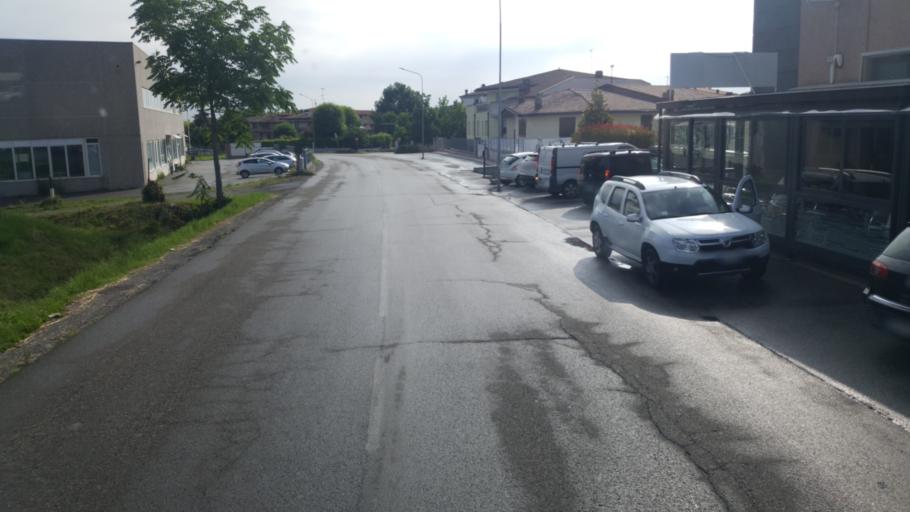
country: IT
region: Emilia-Romagna
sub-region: Provincia di Modena
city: Marano sul Panaro
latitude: 44.4629
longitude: 10.9711
